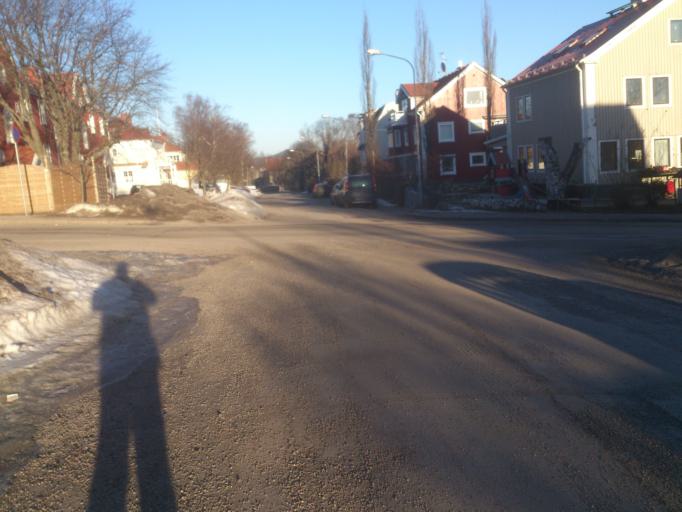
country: SE
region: Vaesternorrland
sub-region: Sundsvalls Kommun
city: Sundsvall
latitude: 62.3828
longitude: 17.3158
